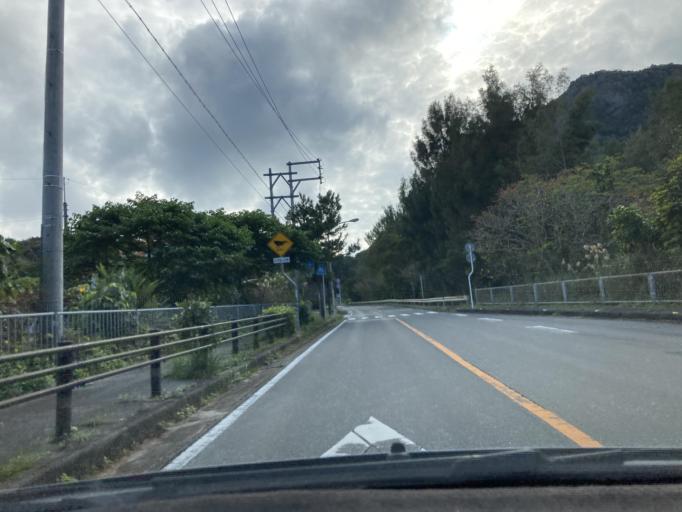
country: JP
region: Okinawa
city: Nago
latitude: 26.8579
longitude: 128.2610
